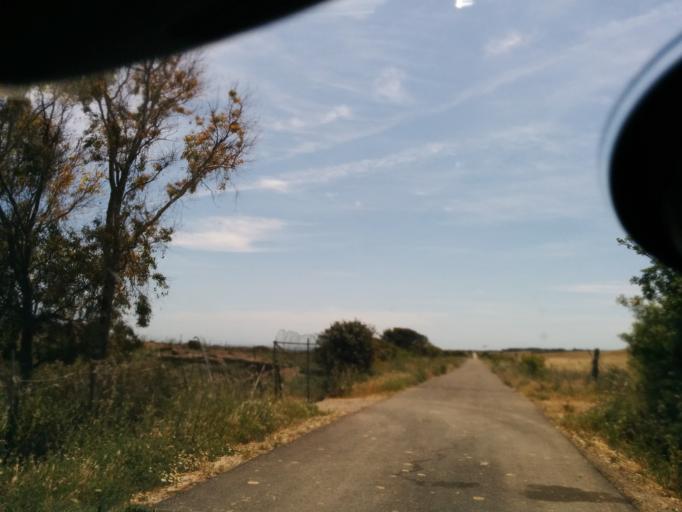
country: IT
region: Sardinia
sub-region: Provincia di Carbonia-Iglesias
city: Calasetta
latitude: 39.0466
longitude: 8.3862
